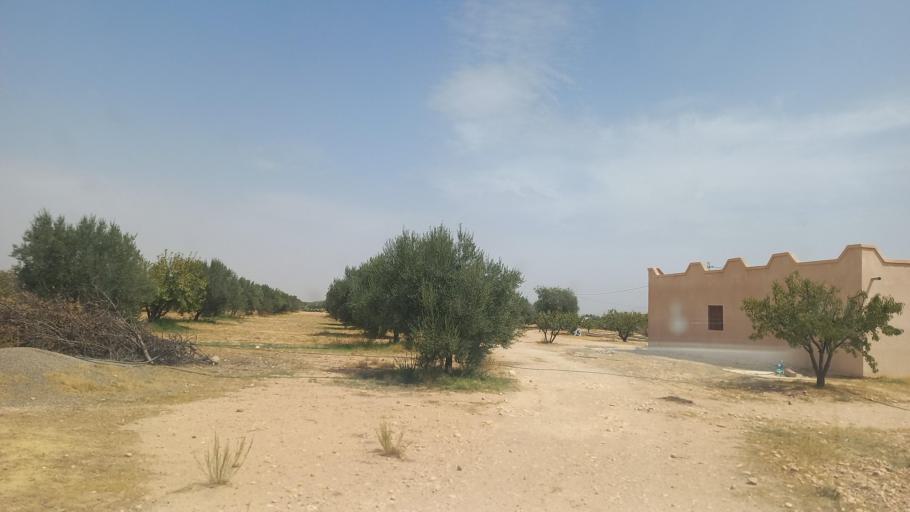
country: TN
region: Al Qasrayn
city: Kasserine
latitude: 35.2571
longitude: 9.0058
